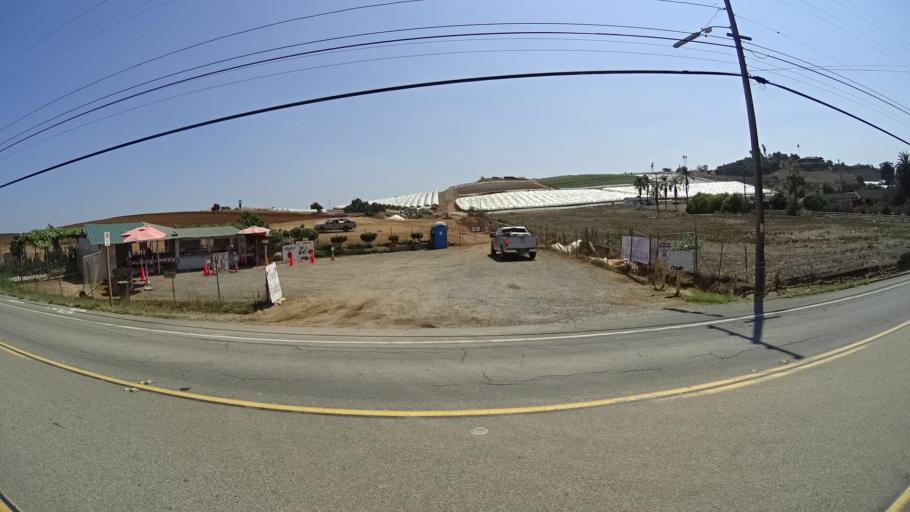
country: US
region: California
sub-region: San Diego County
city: Vista
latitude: 33.2404
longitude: -117.2266
